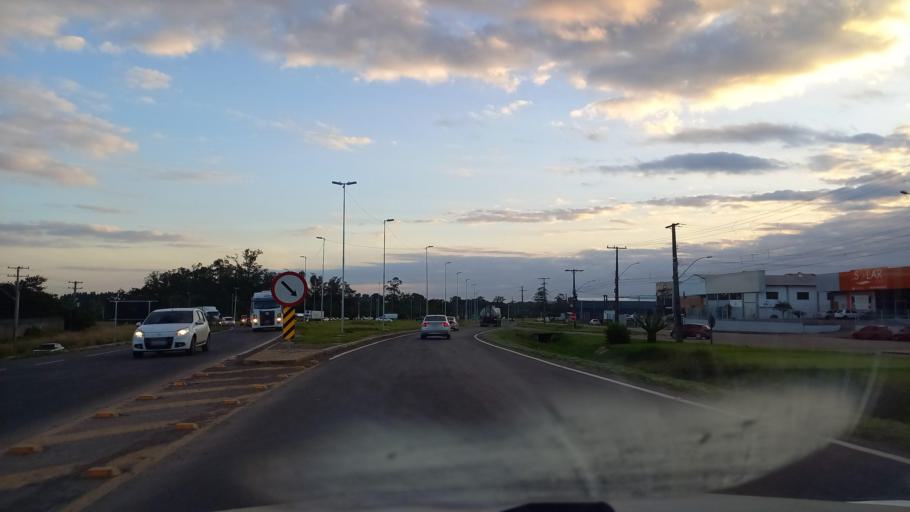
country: BR
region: Rio Grande do Sul
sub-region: Santa Cruz Do Sul
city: Santa Cruz do Sul
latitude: -29.6882
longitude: -52.4478
